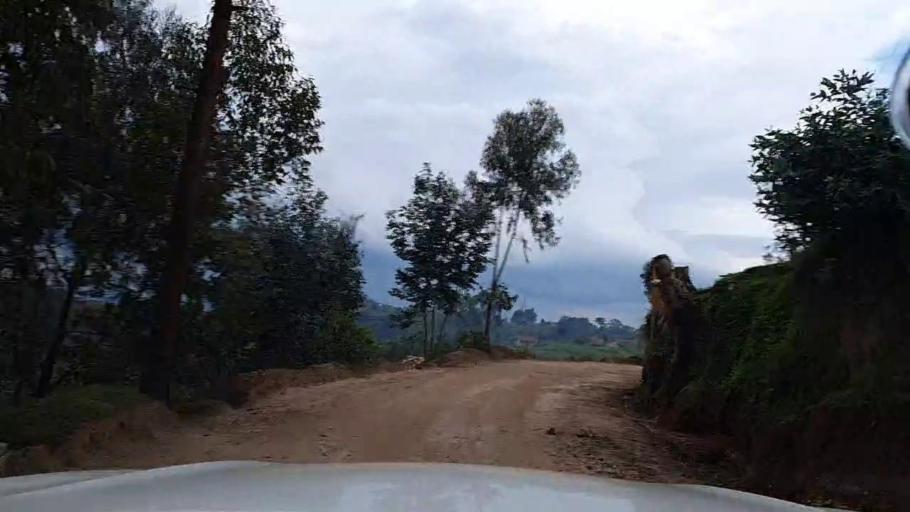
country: BI
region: Kayanza
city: Kayanza
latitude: -2.7984
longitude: 29.4972
